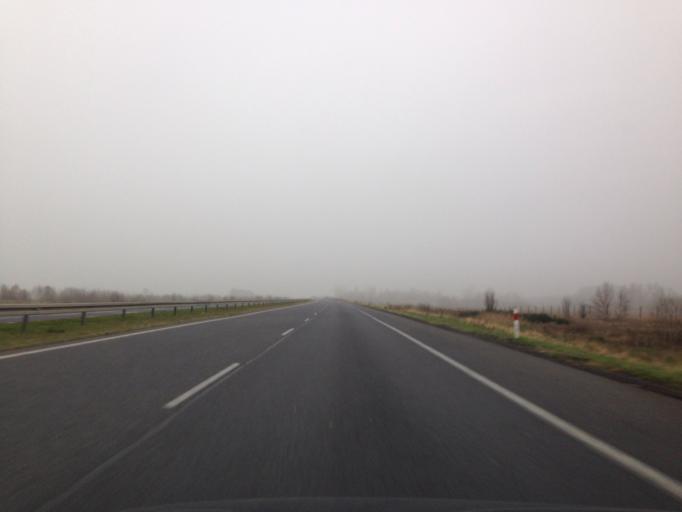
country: PL
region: Lodz Voivodeship
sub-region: Powiat radomszczanski
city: Kamiensk
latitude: 51.2743
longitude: 19.5324
